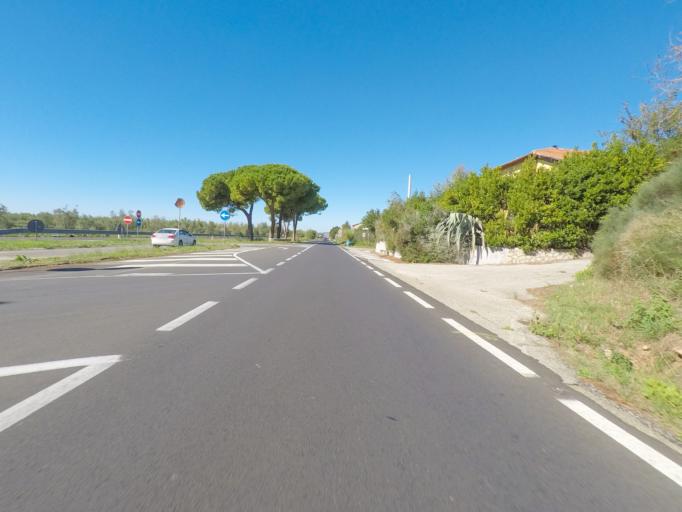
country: IT
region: Tuscany
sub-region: Provincia di Grosseto
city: Orbetello Scalo
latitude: 42.4549
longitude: 11.2511
